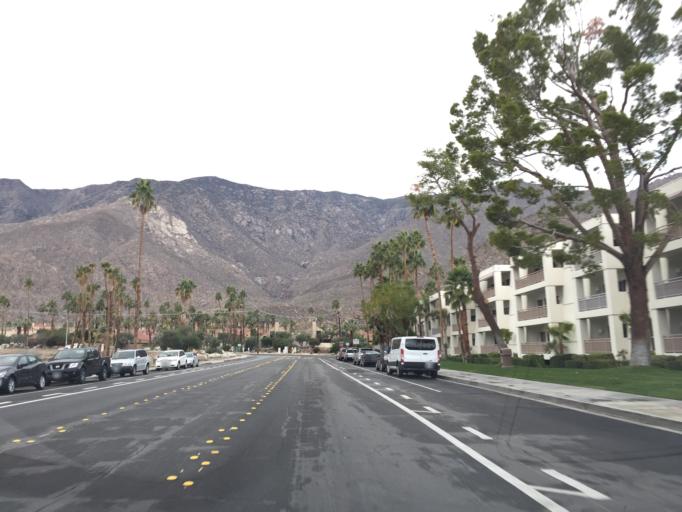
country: US
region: California
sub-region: Riverside County
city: Palm Springs
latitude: 33.7805
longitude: -116.5438
